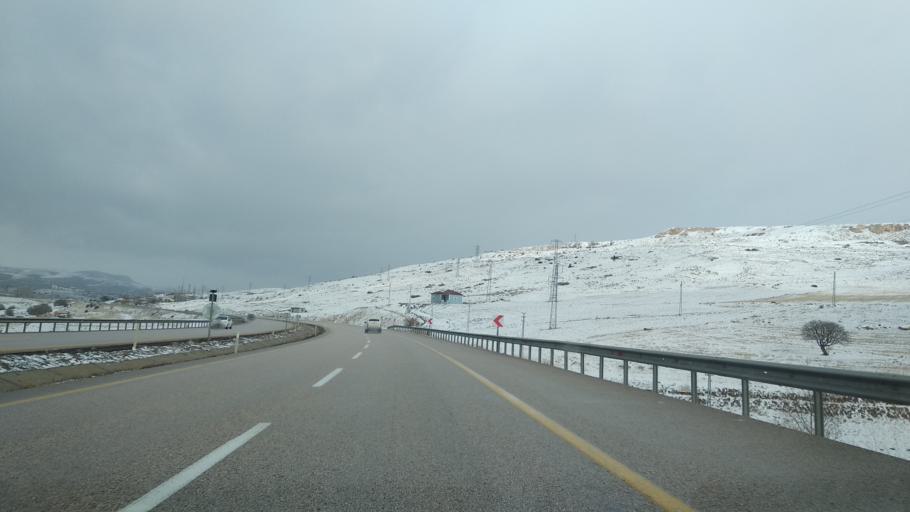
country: TR
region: Kayseri
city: Pinarbasi
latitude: 38.7017
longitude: 36.3719
